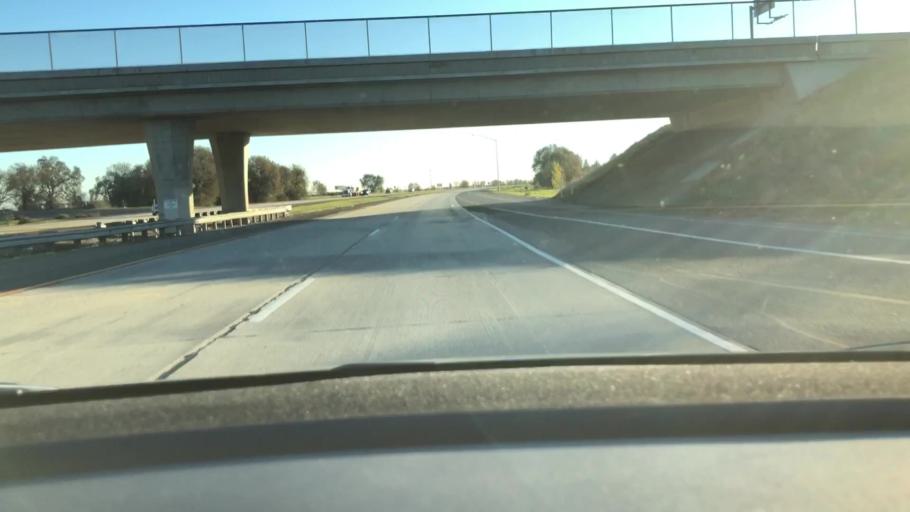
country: US
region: California
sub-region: Yolo County
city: Woodland
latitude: 38.6631
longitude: -121.7516
